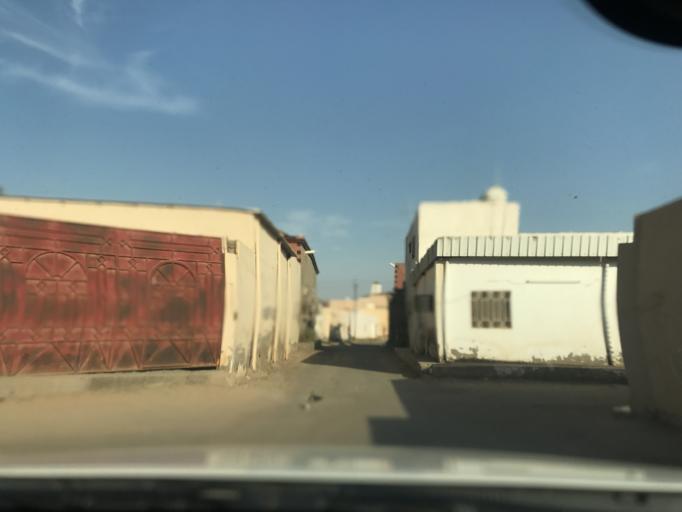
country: SA
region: Makkah
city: Al Jumum
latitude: 21.4400
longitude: 39.5230
